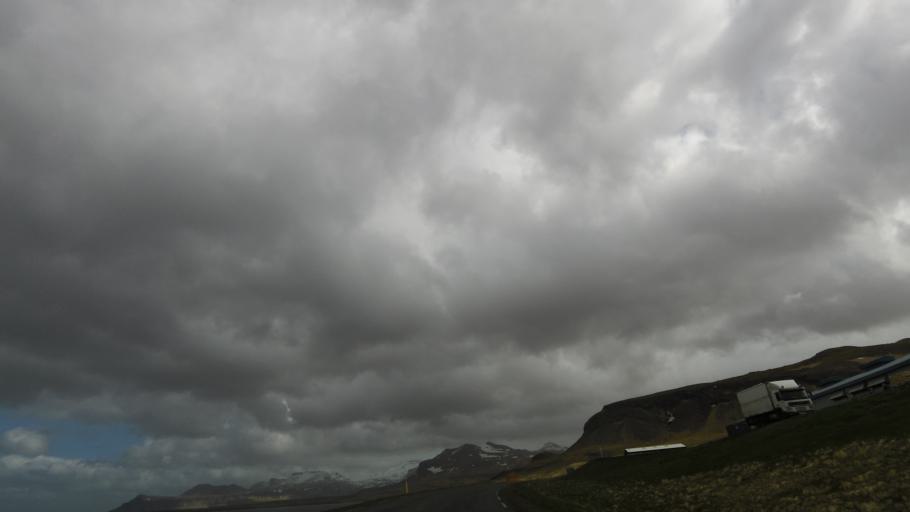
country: IS
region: West
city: Olafsvik
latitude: 64.8918
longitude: -23.6766
